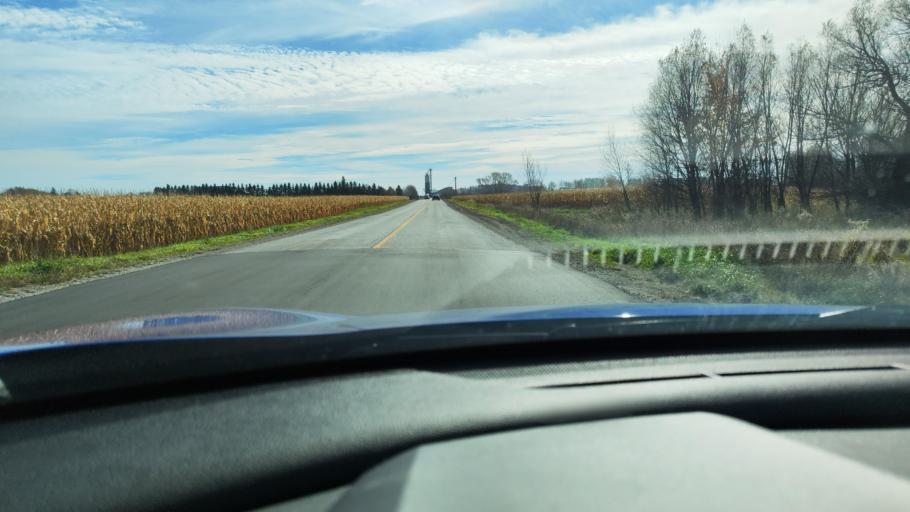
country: CA
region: Ontario
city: Wasaga Beach
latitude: 44.4460
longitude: -79.9999
